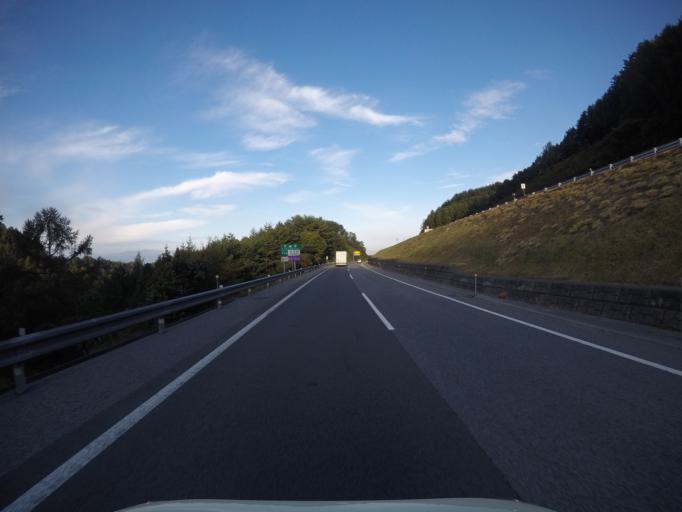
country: JP
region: Nagano
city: Saku
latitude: 36.2700
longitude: 138.5230
